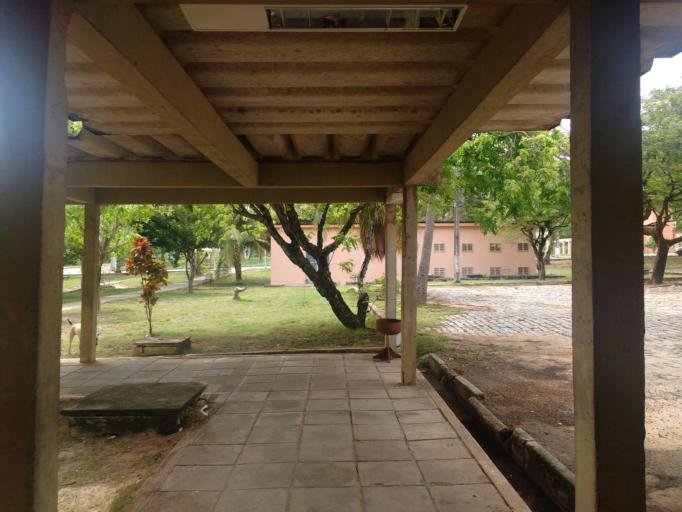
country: BR
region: Ceara
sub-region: Fortaleza
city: Fortaleza
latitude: -3.7474
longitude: -38.5764
